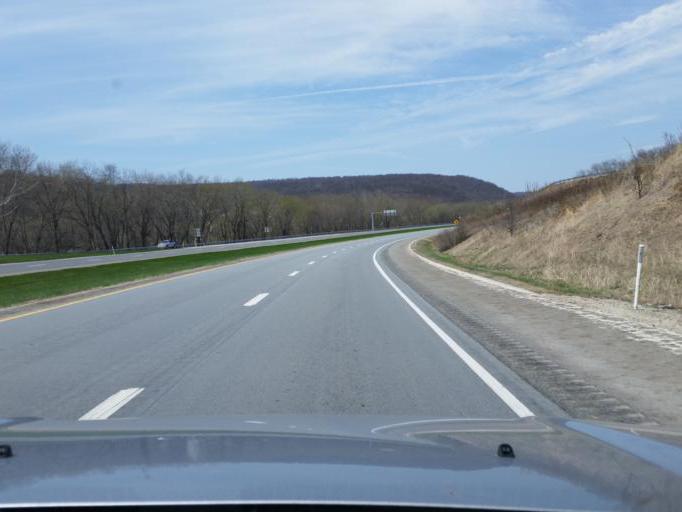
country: US
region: Pennsylvania
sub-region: Perry County
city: Newport
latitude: 40.5434
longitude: -77.1505
